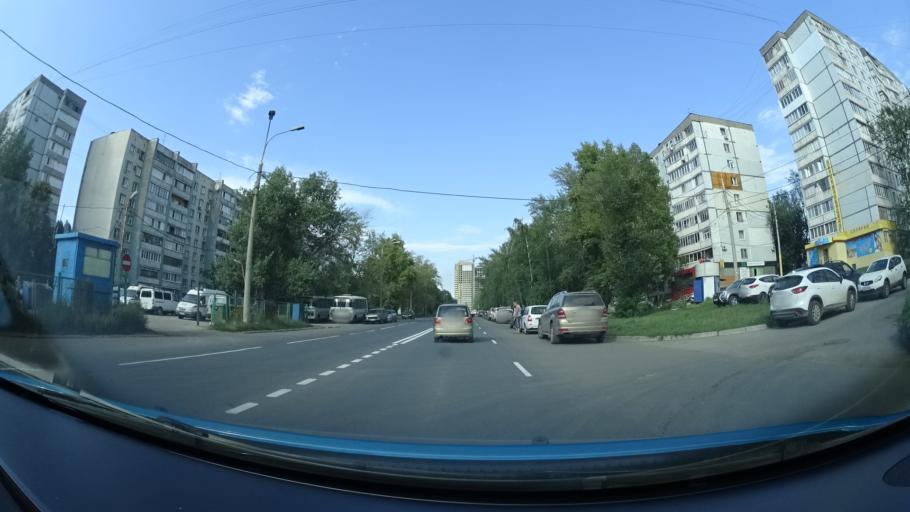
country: RU
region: Samara
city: Samara
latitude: 53.2621
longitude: 50.2250
